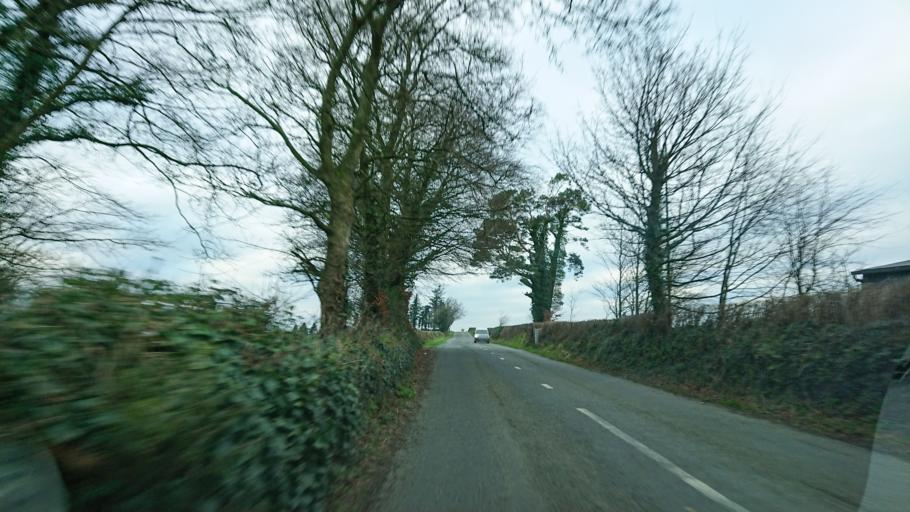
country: IE
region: Munster
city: Carrick-on-Suir
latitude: 52.3021
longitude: -7.4849
